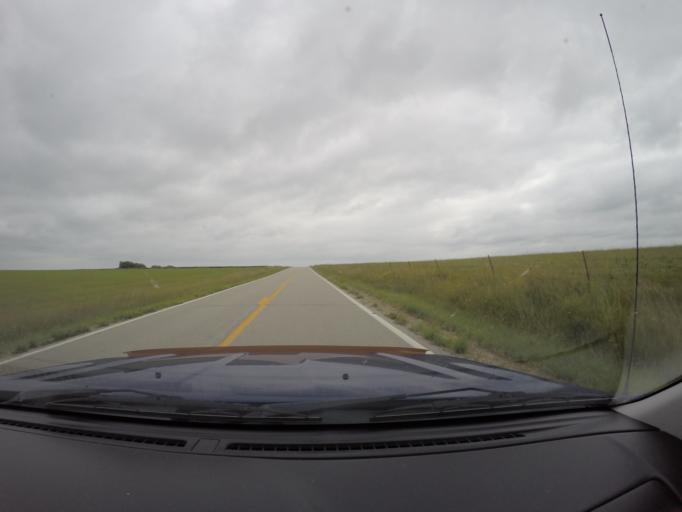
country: US
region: Kansas
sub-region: Morris County
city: Council Grove
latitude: 38.8035
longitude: -96.5942
